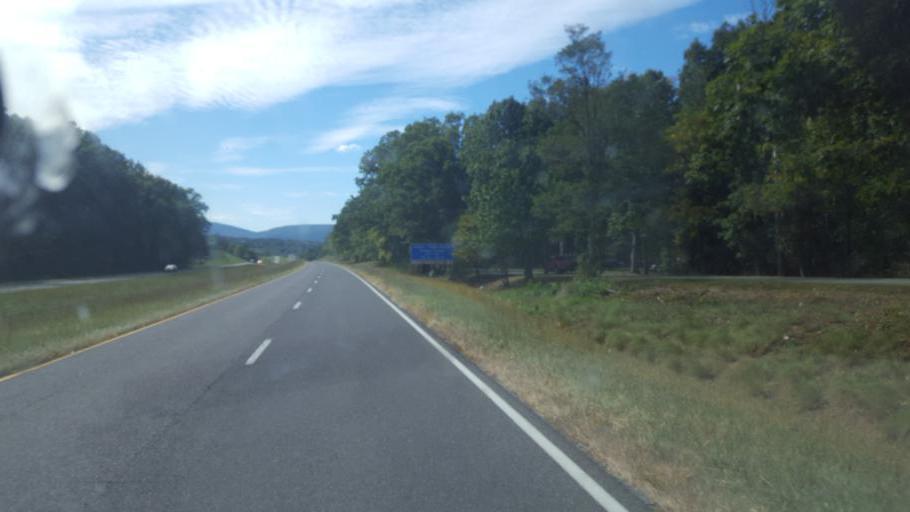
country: US
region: Virginia
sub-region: Page County
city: Luray
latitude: 38.6764
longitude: -78.4339
